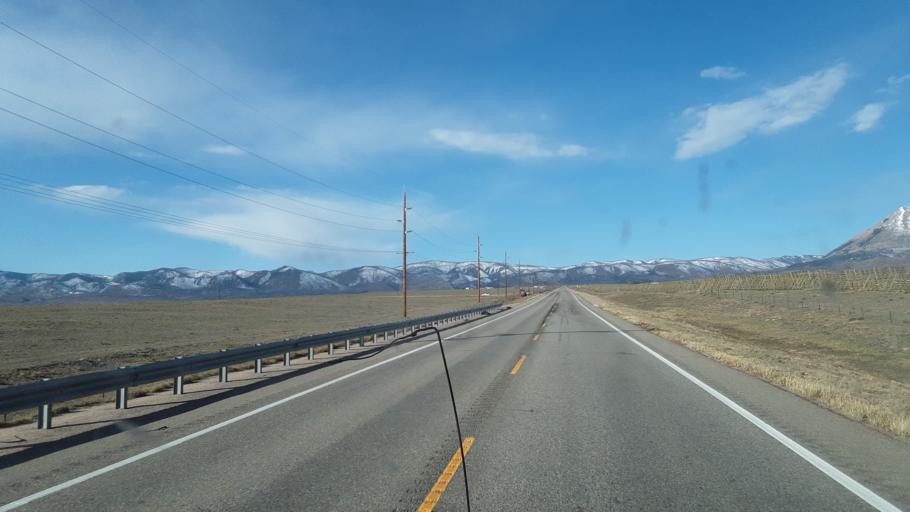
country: US
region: Colorado
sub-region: Huerfano County
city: Walsenburg
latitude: 37.5439
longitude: -105.0096
